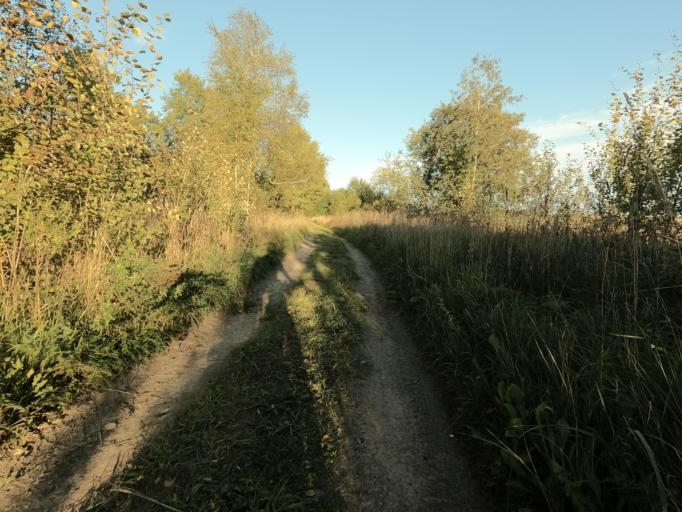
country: RU
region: Leningrad
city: Nikol'skoye
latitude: 59.7006
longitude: 30.7437
